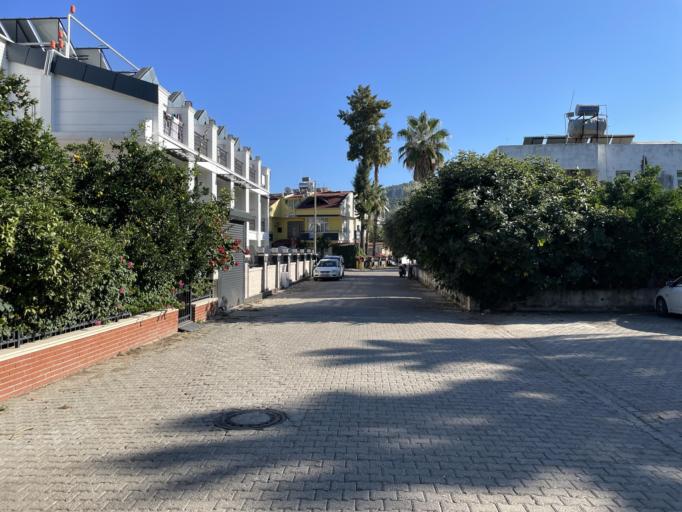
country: TR
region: Antalya
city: Kemer
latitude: 36.6026
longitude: 30.5636
